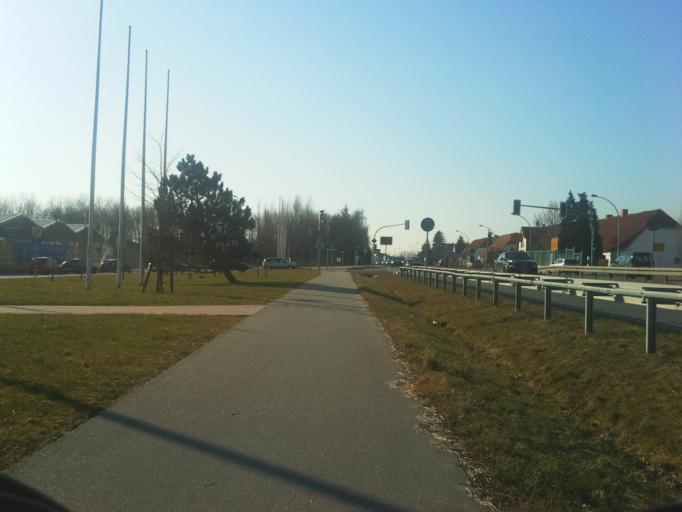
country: DE
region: Mecklenburg-Vorpommern
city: Lambrechtshagen
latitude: 54.1081
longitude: 12.0294
